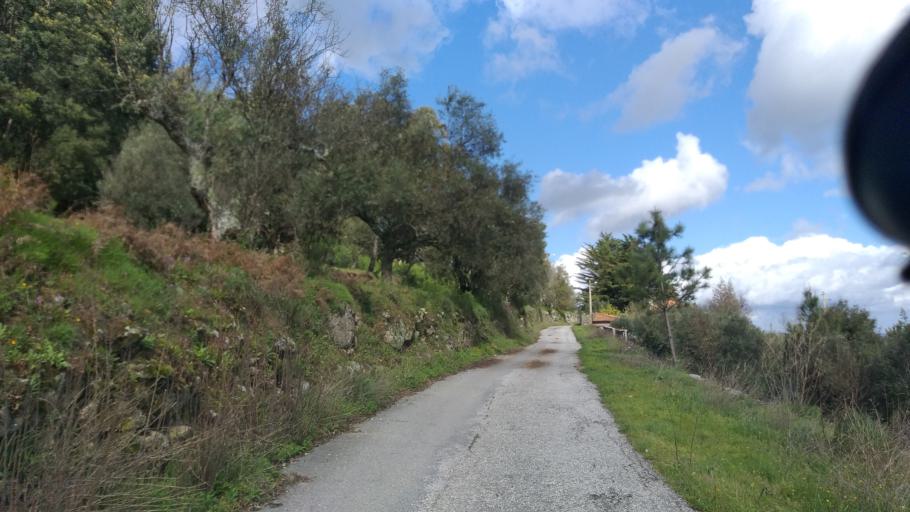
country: PT
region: Guarda
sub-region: Fornos de Algodres
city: Fornos de Algodres
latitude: 40.6172
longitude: -7.5450
